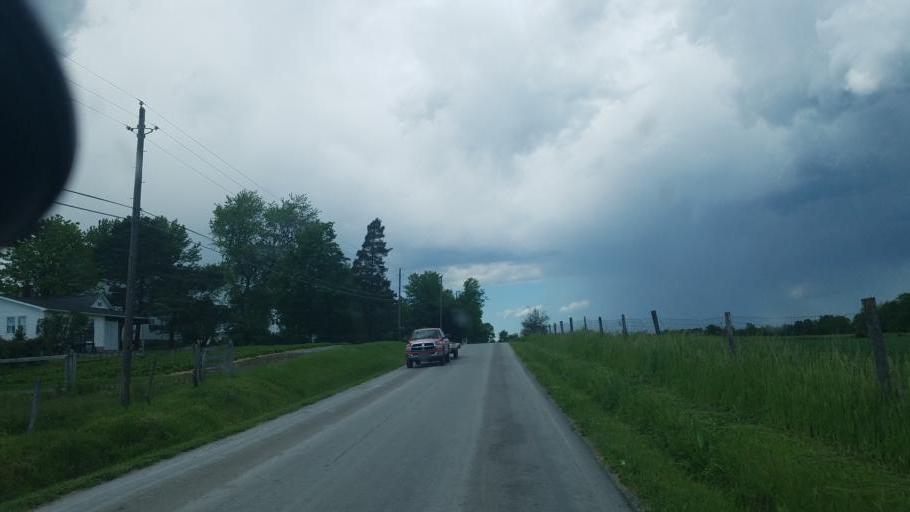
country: US
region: Ohio
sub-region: Geauga County
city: Middlefield
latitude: 41.4664
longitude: -81.0032
